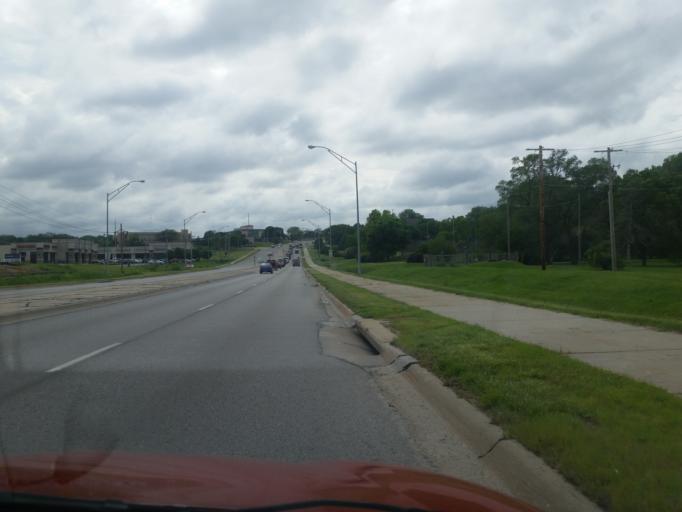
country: US
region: Nebraska
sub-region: Sarpy County
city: Offutt Air Force Base
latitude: 41.1182
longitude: -95.9412
